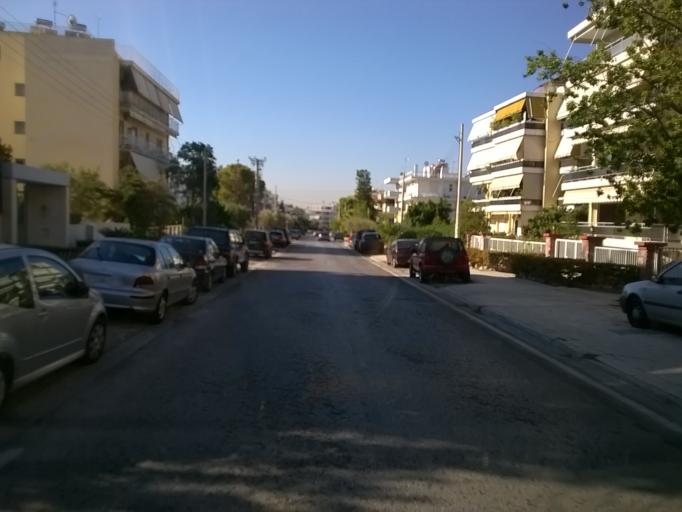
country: GR
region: Attica
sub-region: Nomarchia Athinas
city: Glyfada
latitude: 37.8684
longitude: 23.7532
